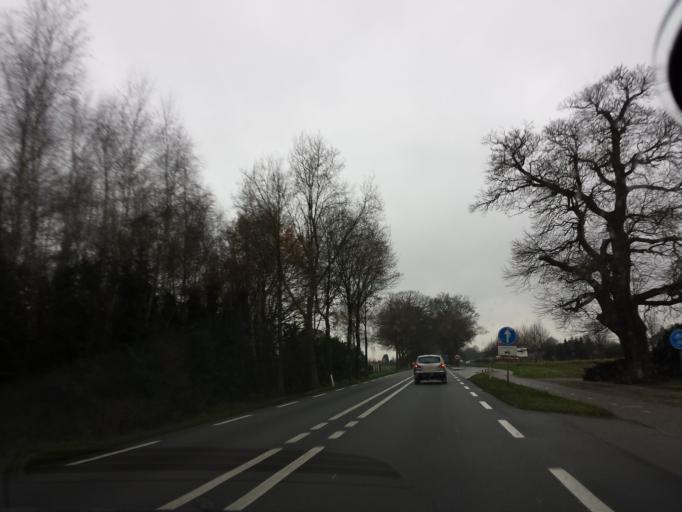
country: NL
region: Limburg
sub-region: Gemeente Beesel
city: Reuver
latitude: 51.2991
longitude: 6.0539
